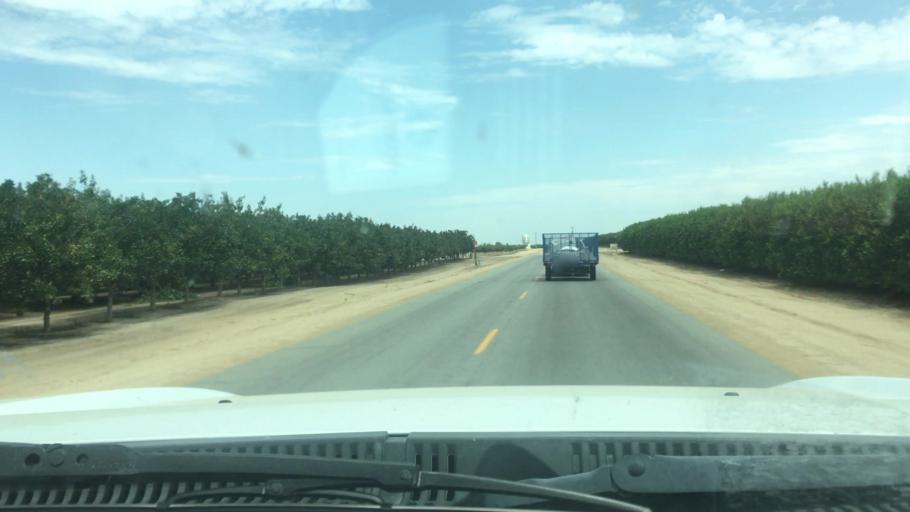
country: US
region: California
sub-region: Kern County
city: McFarland
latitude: 35.5864
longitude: -119.1511
